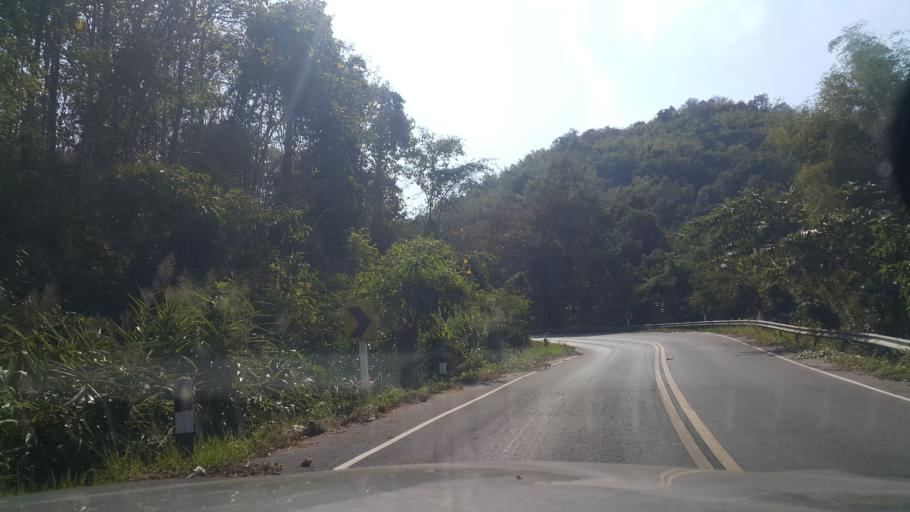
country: TH
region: Loei
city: Pak Chom
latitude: 18.1023
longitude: 102.0461
